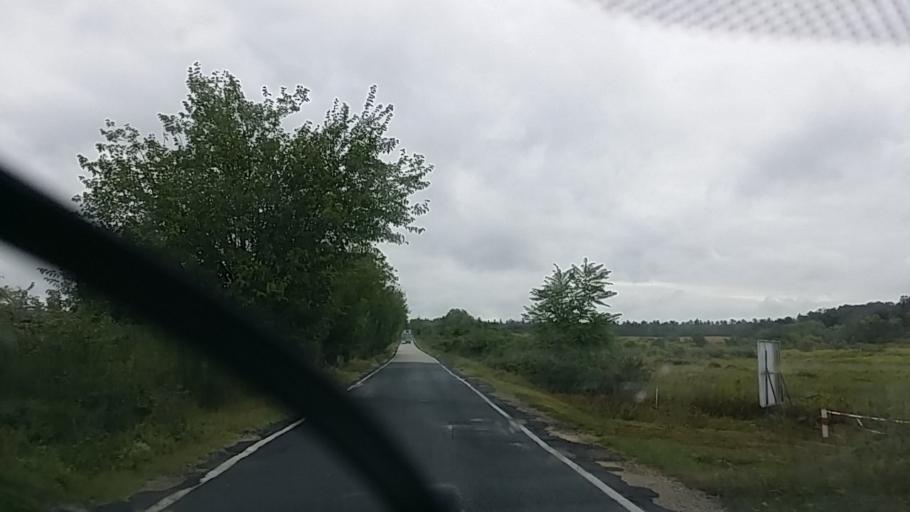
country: HU
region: Gyor-Moson-Sopron
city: Fertorakos
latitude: 47.7495
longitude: 16.6217
